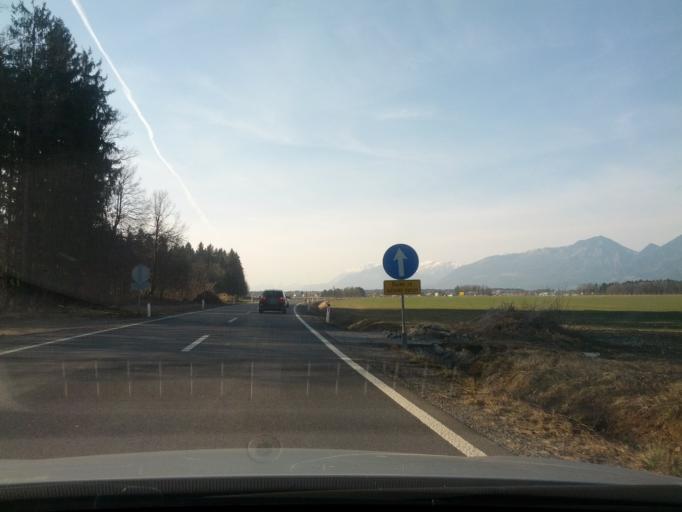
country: SI
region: Sencur
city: Sencur
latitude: 46.2300
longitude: 14.4366
